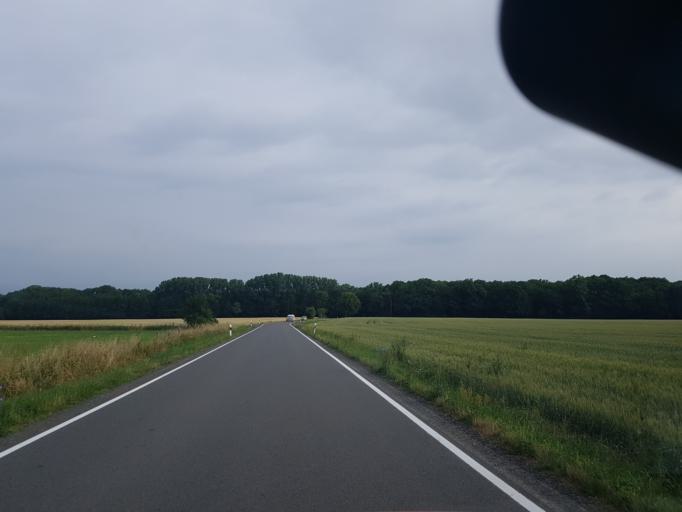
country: DE
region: Brandenburg
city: Sonnewalde
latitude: 51.6933
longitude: 13.6253
